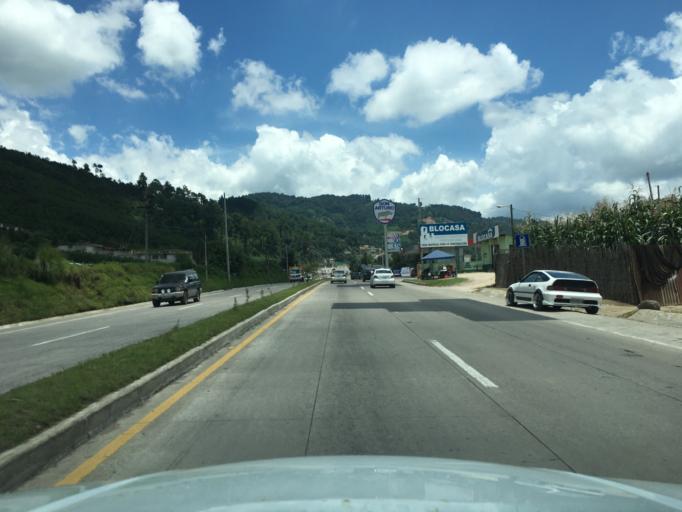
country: GT
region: Chimaltenango
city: Tecpan Guatemala
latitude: 14.7747
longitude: -90.9880
